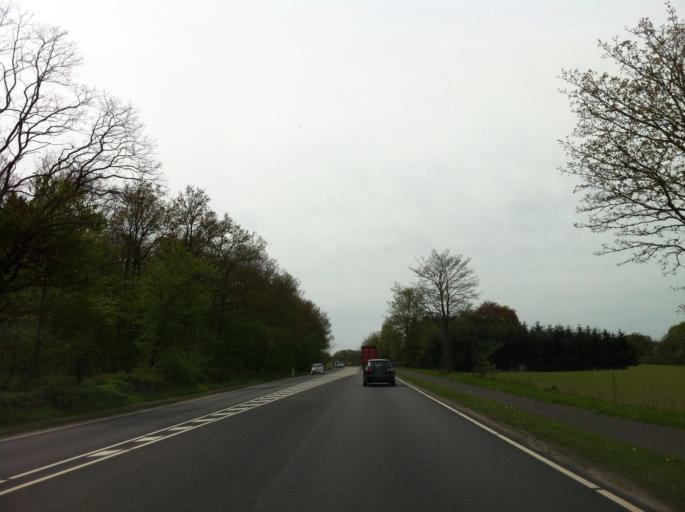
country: DK
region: Zealand
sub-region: Lejre Kommune
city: Osted
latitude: 55.5348
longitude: 11.9210
